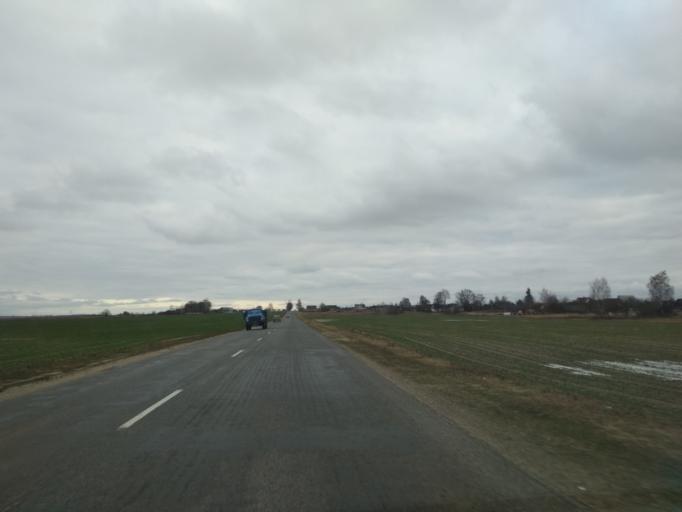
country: BY
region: Minsk
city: Svislach
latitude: 53.5698
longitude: 27.9954
